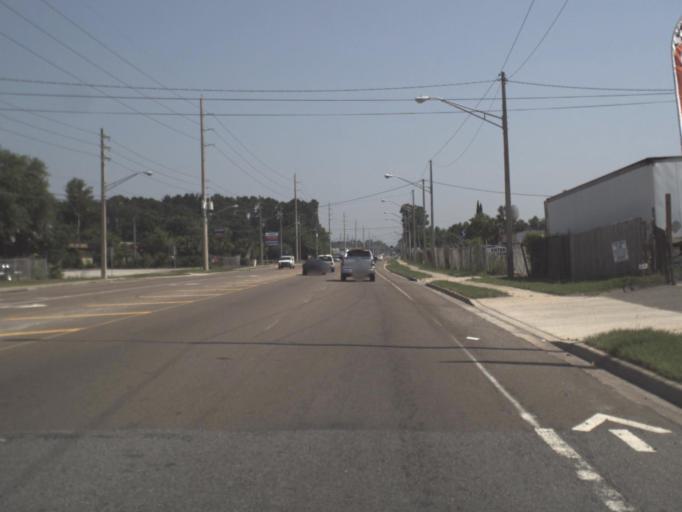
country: US
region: Florida
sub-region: Duval County
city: Jacksonville
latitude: 30.3247
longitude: -81.7519
